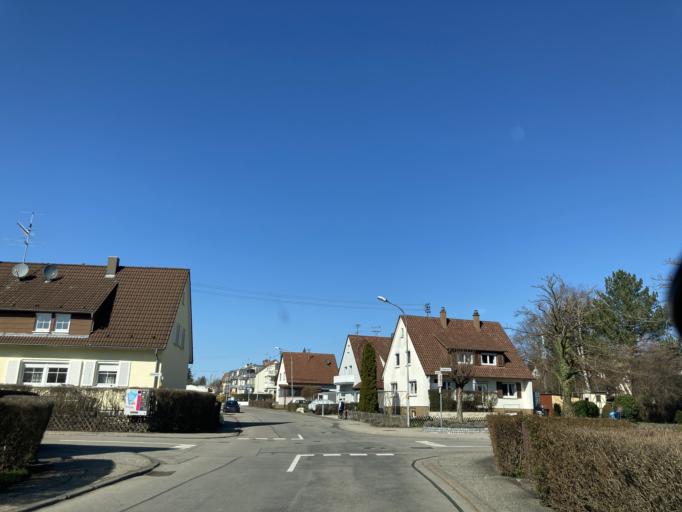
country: DE
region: Baden-Wuerttemberg
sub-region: Tuebingen Region
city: Bodelshausen
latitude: 48.3940
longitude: 8.9771
